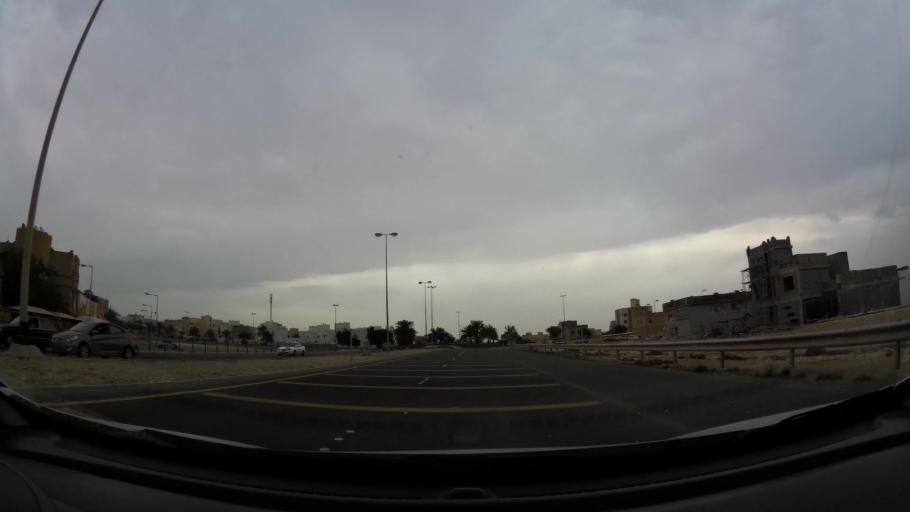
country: BH
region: Central Governorate
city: Madinat Hamad
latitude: 26.1043
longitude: 50.4979
